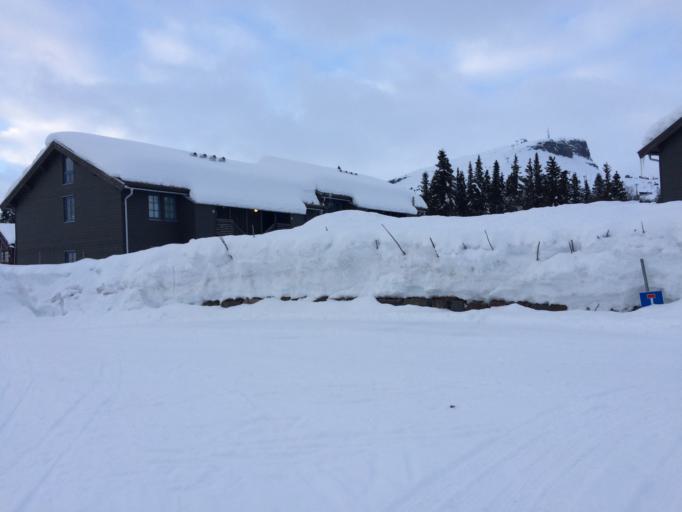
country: NO
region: Oppland
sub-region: Gausdal
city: Segalstad bru
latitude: 61.3339
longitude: 10.0881
